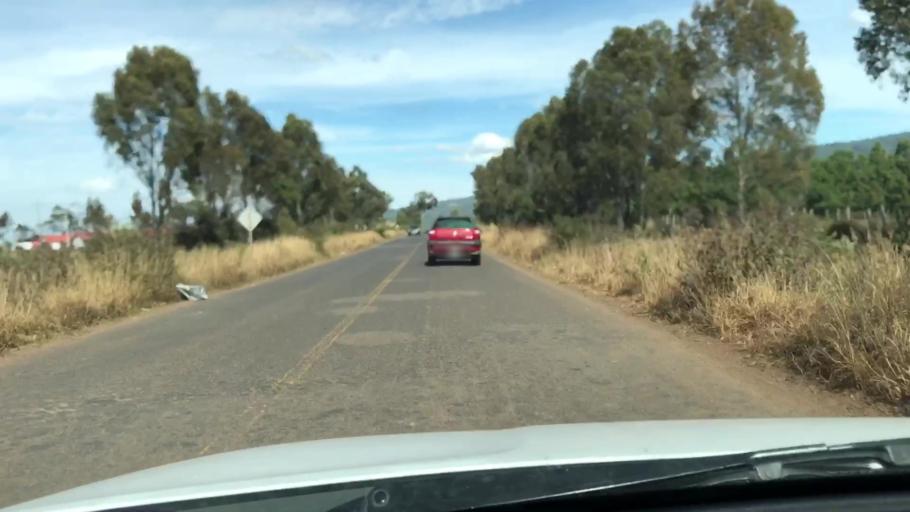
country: MX
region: Jalisco
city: Chiquilistlan
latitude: 20.1276
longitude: -103.7224
